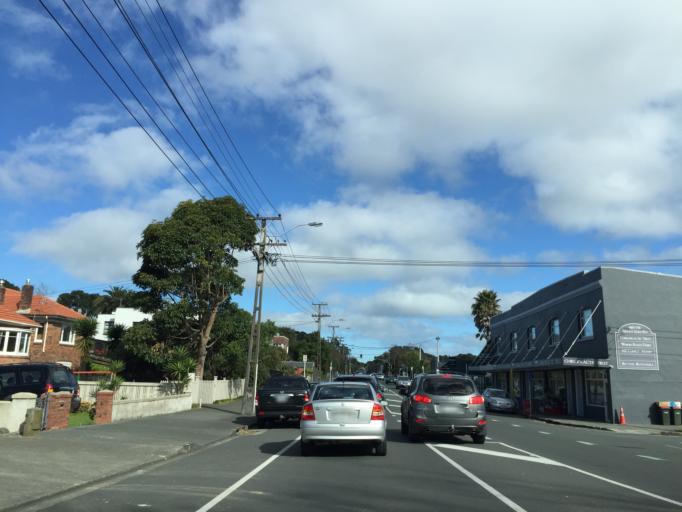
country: NZ
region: Auckland
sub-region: Auckland
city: Auckland
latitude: -36.8915
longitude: 174.7594
